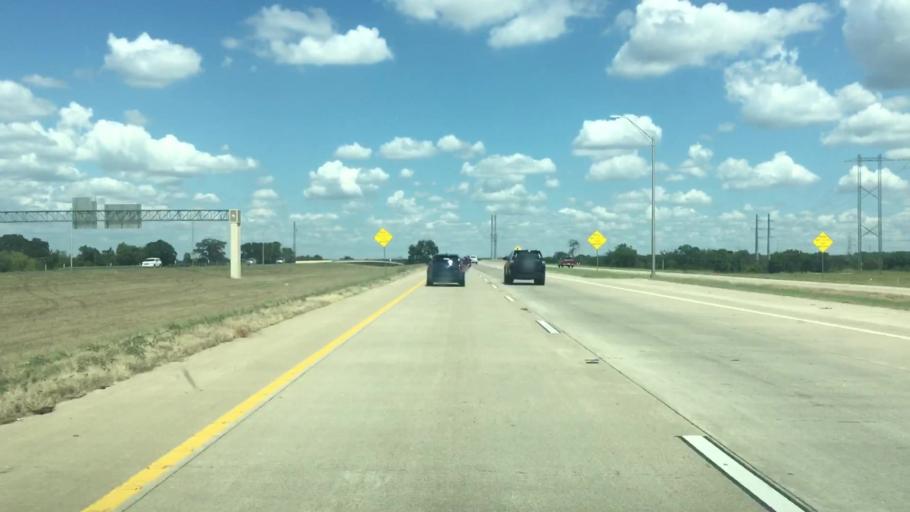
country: US
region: Texas
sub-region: Travis County
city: Hornsby Bend
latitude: 30.2059
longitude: -97.6223
